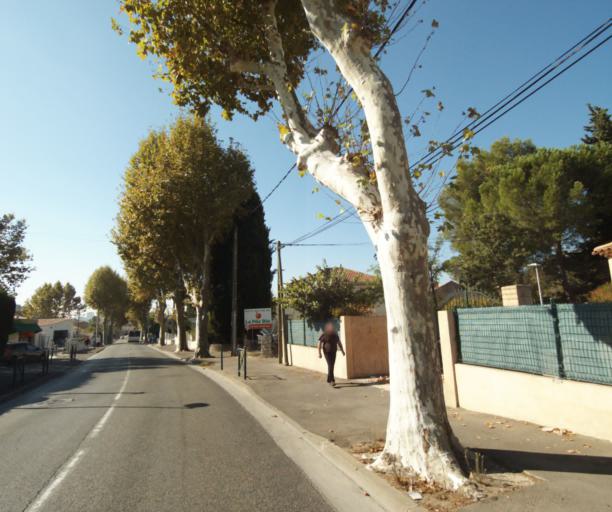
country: FR
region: Provence-Alpes-Cote d'Azur
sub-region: Departement des Bouches-du-Rhone
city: Plan-de-Cuques
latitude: 43.3431
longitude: 5.4576
